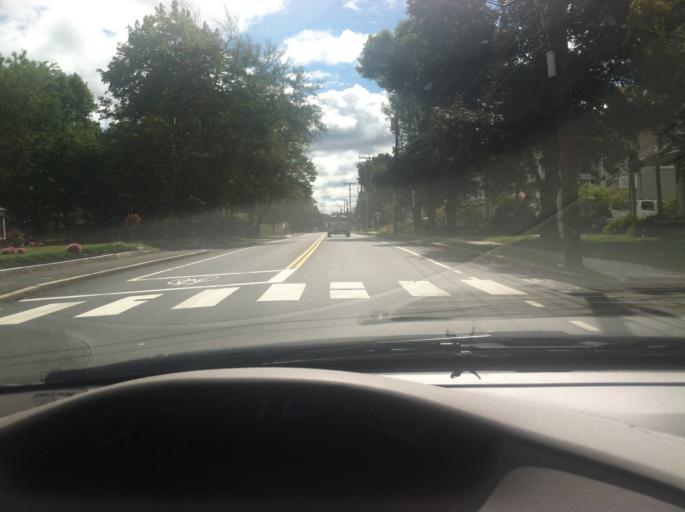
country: US
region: Massachusetts
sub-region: Middlesex County
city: Lexington
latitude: 42.4567
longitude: -71.2359
